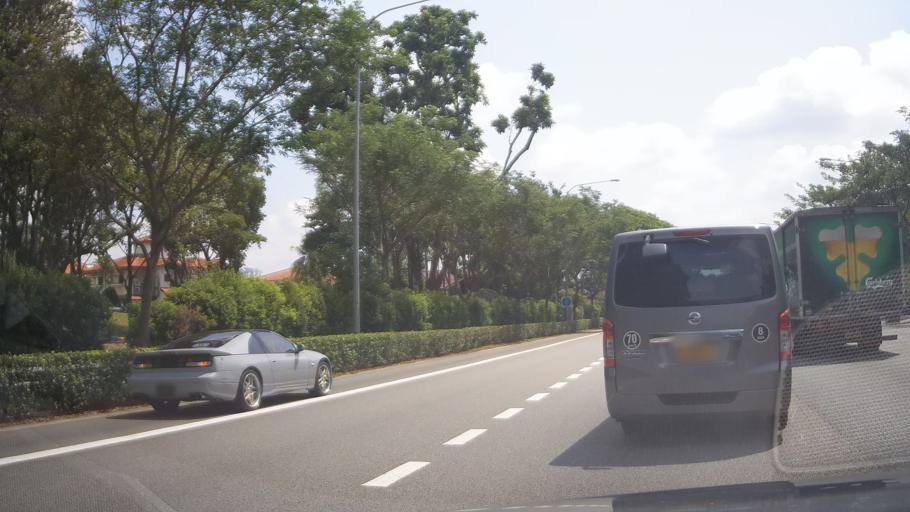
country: SG
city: Singapore
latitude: 1.3330
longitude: 103.7701
